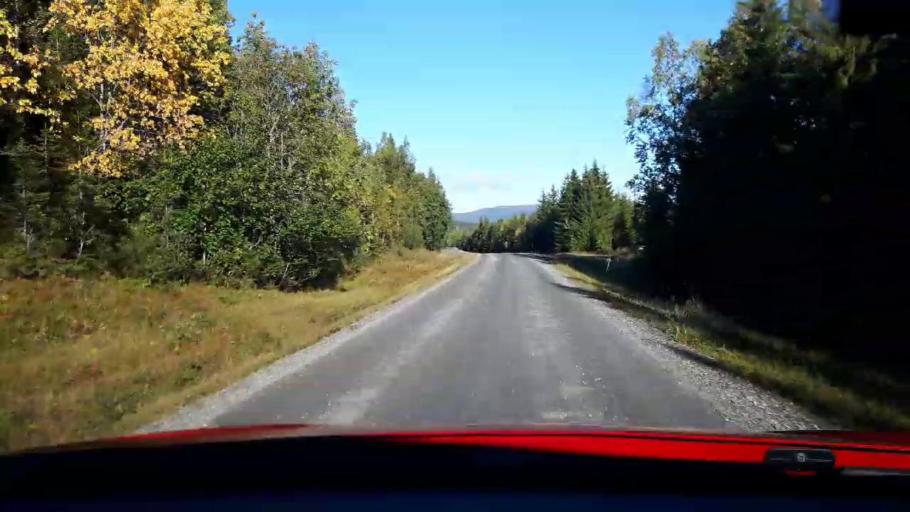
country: NO
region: Nord-Trondelag
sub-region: Lierne
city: Sandvika
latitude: 64.5824
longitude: 13.8886
